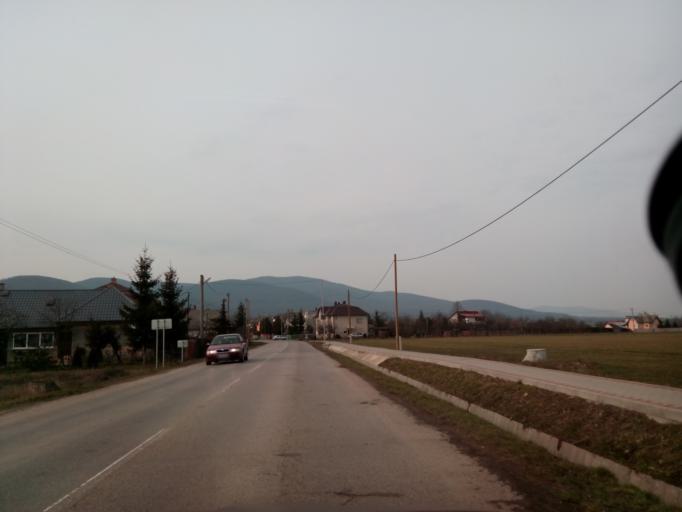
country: SK
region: Kosicky
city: Secovce
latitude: 48.6439
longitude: 21.5778
